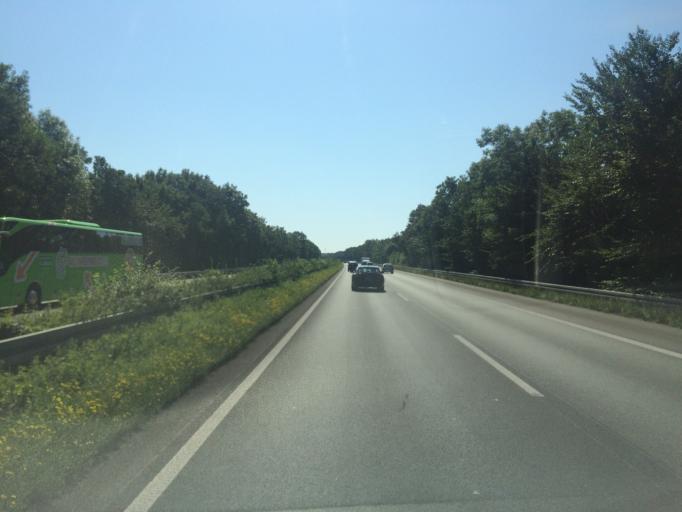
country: DE
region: North Rhine-Westphalia
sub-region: Regierungsbezirk Munster
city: Ascheberg
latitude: 51.7668
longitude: 7.6410
